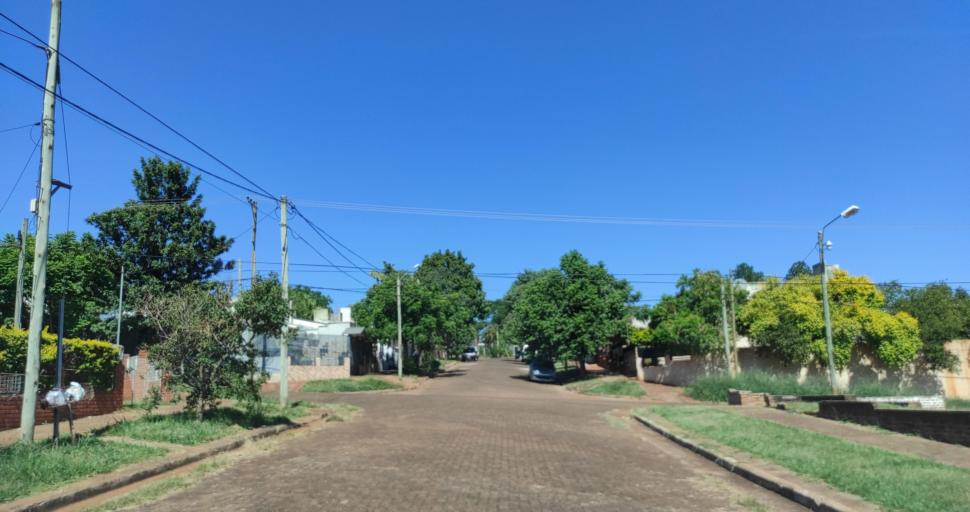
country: AR
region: Misiones
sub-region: Departamento de Capital
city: Posadas
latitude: -27.3979
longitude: -55.9449
